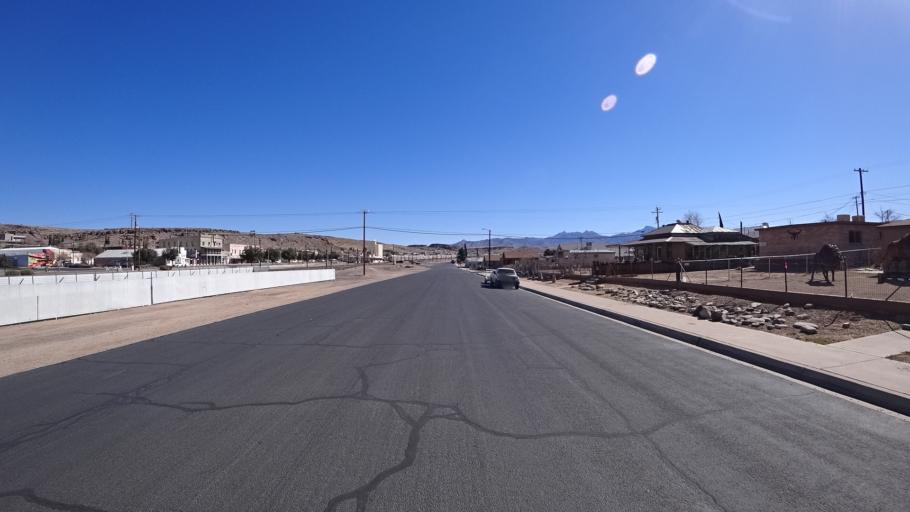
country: US
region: Arizona
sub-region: Mohave County
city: Kingman
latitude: 35.1880
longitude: -114.0558
